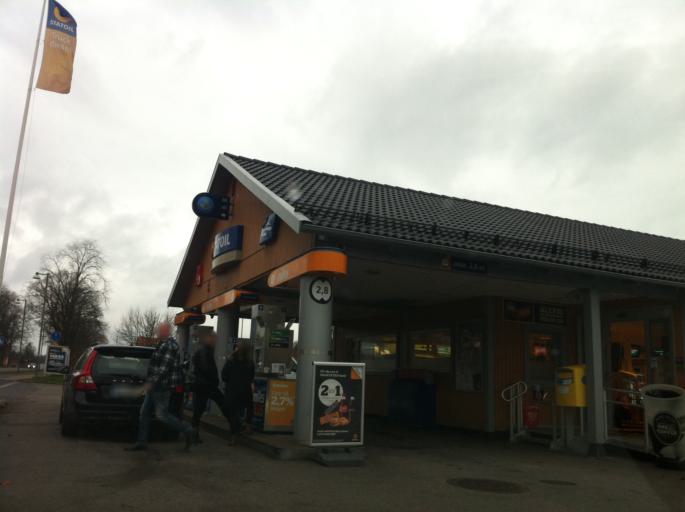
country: SE
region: Joenkoeping
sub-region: Savsjo Kommun
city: Vrigstad
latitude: 57.3729
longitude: 14.5285
